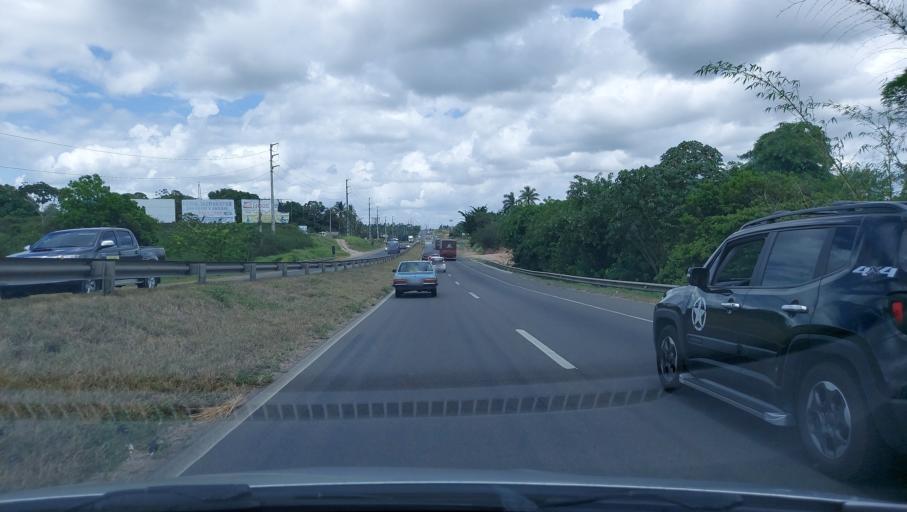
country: BR
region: Bahia
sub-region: Conceicao Do Jacuipe
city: Conceicao do Jacuipe
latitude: -12.3277
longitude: -38.8622
